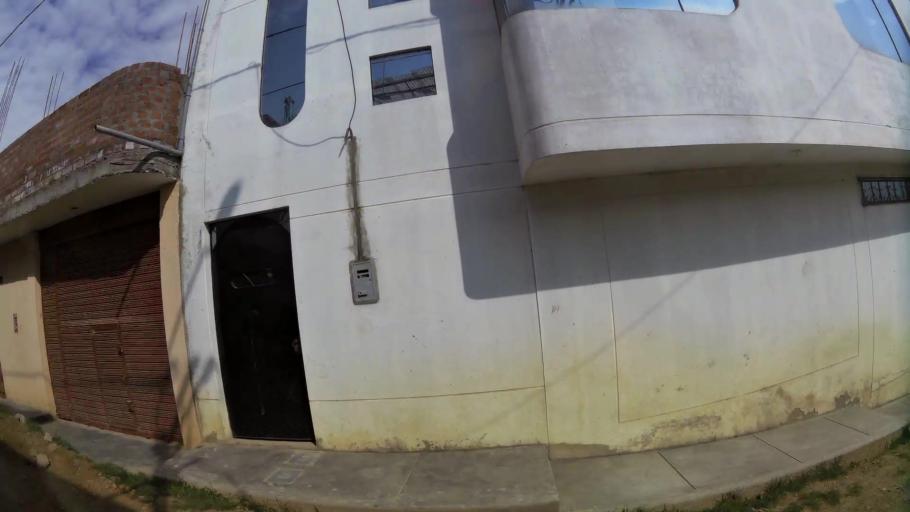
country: PE
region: Junin
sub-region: Provincia de Huancayo
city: Huancayo
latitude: -12.0552
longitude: -75.1934
